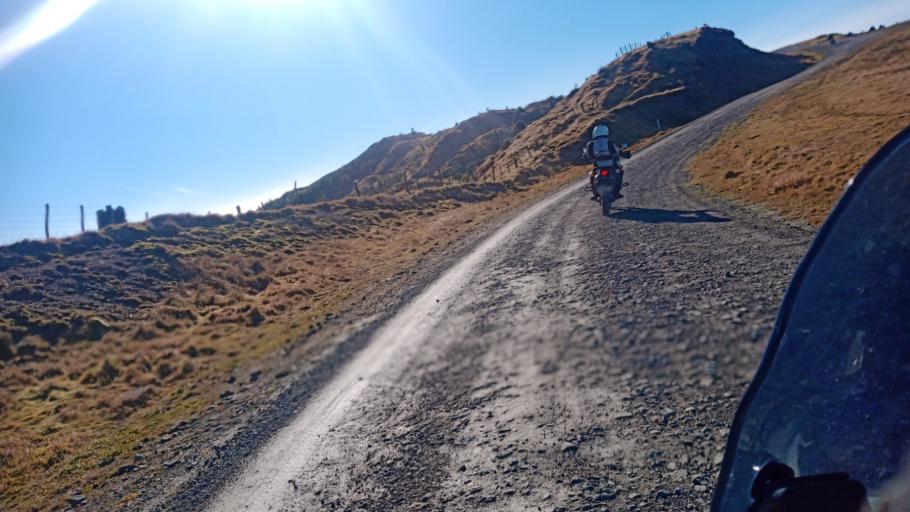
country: NZ
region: Gisborne
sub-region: Gisborne District
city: Gisborne
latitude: -38.1806
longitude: 177.8234
